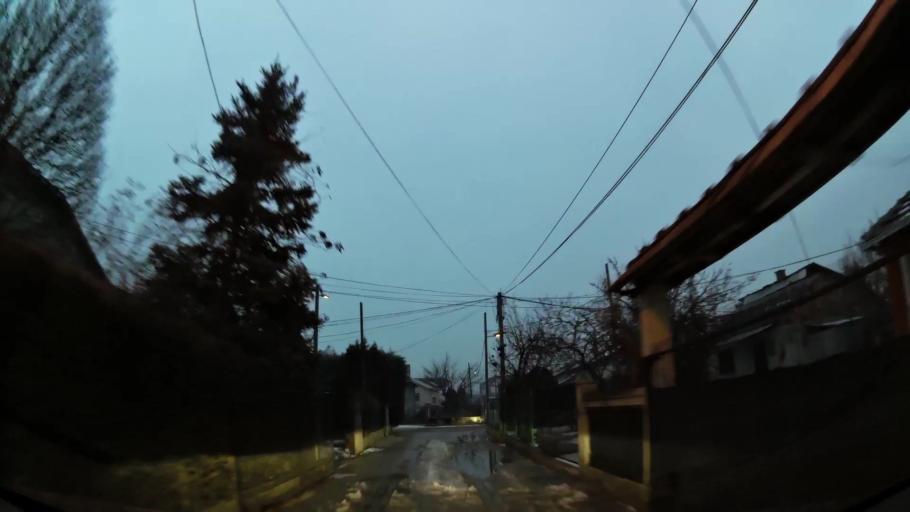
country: MK
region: Kisela Voda
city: Kisela Voda
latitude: 41.9752
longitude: 21.4941
